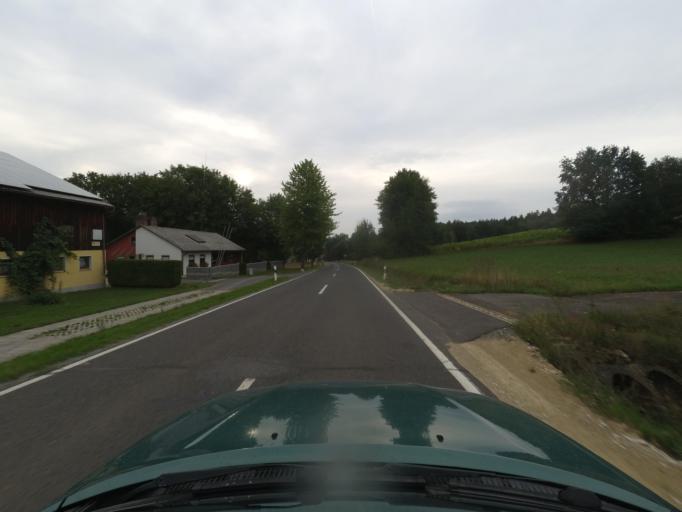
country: DE
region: Bavaria
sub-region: Upper Palatinate
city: Edelsfeld
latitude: 49.5793
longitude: 11.7164
